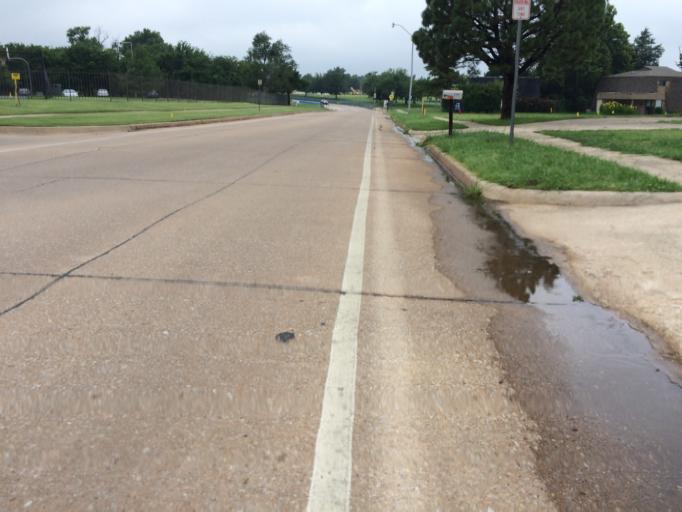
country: US
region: Oklahoma
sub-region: Cleveland County
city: Norman
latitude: 35.2090
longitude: -97.4157
